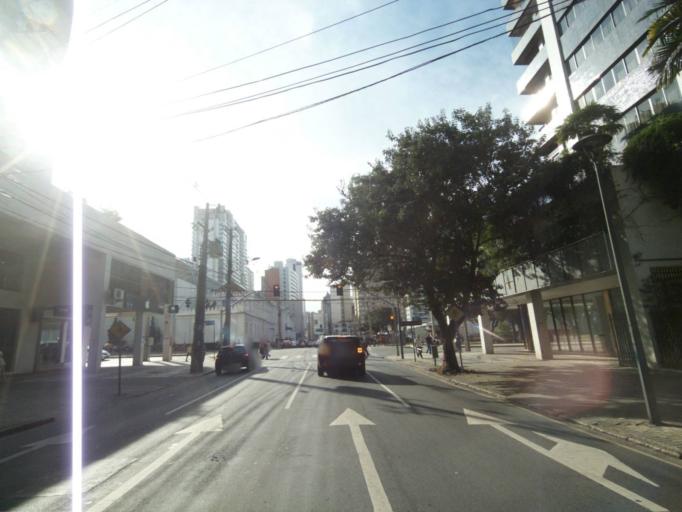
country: BR
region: Parana
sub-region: Curitiba
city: Curitiba
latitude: -25.4418
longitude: -49.2763
